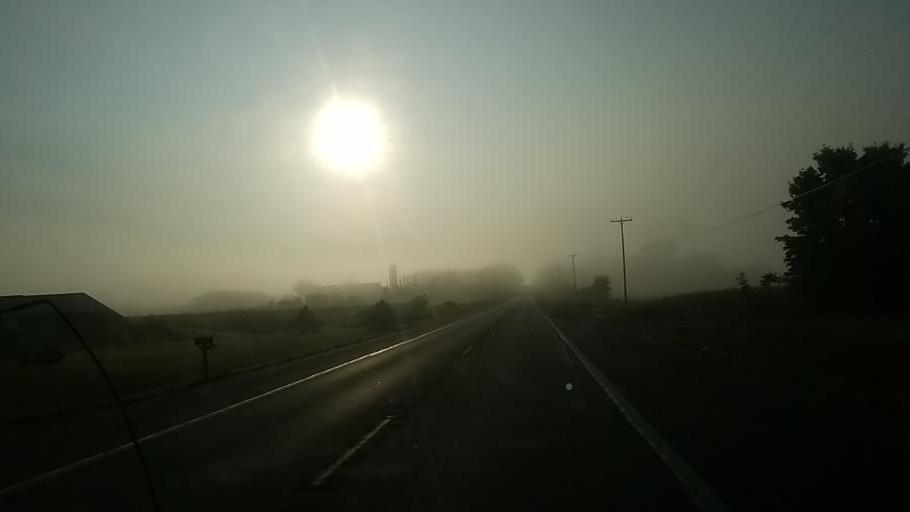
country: US
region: Michigan
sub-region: Newaygo County
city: Fremont
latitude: 43.4673
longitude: -86.0139
